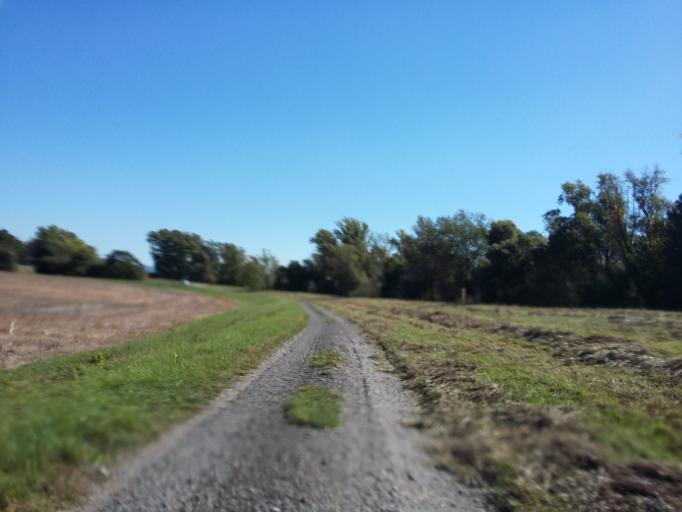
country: AT
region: Lower Austria
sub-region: Politischer Bezirk Ganserndorf
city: Marchegg
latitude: 48.2989
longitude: 16.9233
